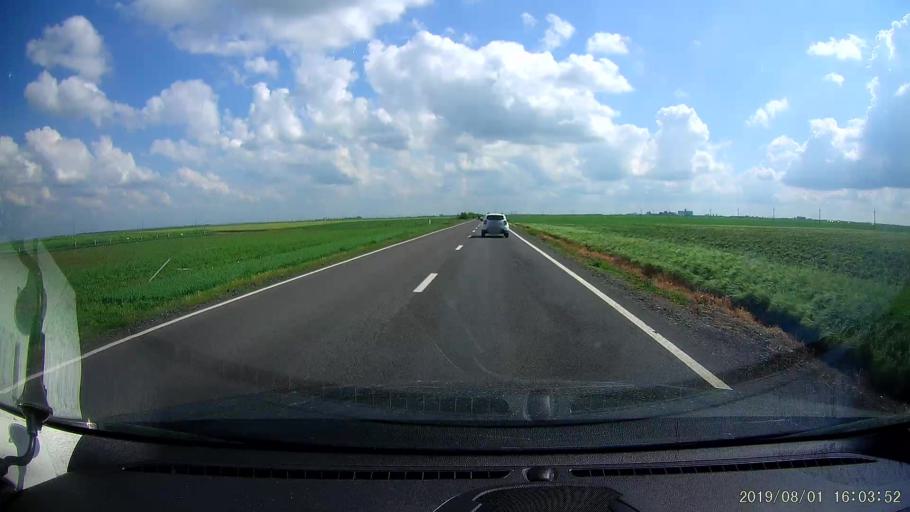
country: RO
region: Calarasi
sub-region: Comuna Dragalina
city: Drajna Noua
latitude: 44.4618
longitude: 27.3826
